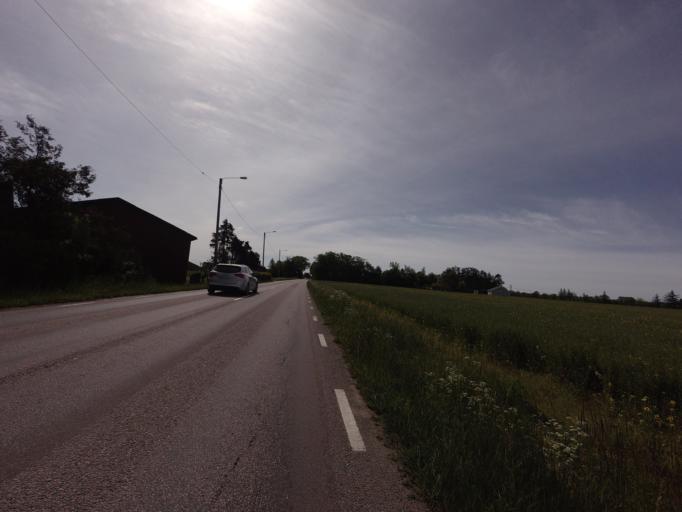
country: SE
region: Skane
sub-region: Helsingborg
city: Odakra
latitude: 56.1453
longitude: 12.6815
